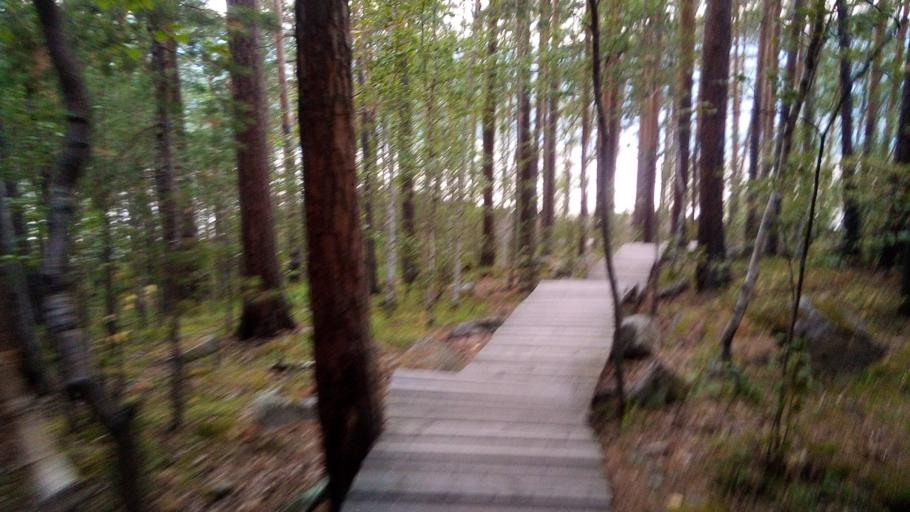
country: RU
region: Chelyabinsk
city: Turgoyak
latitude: 55.1617
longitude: 60.0310
